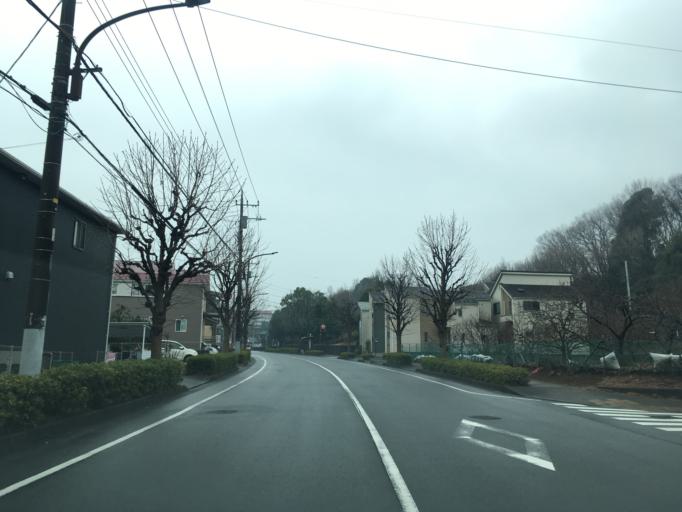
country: JP
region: Tokyo
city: Hino
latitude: 35.6186
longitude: 139.4276
